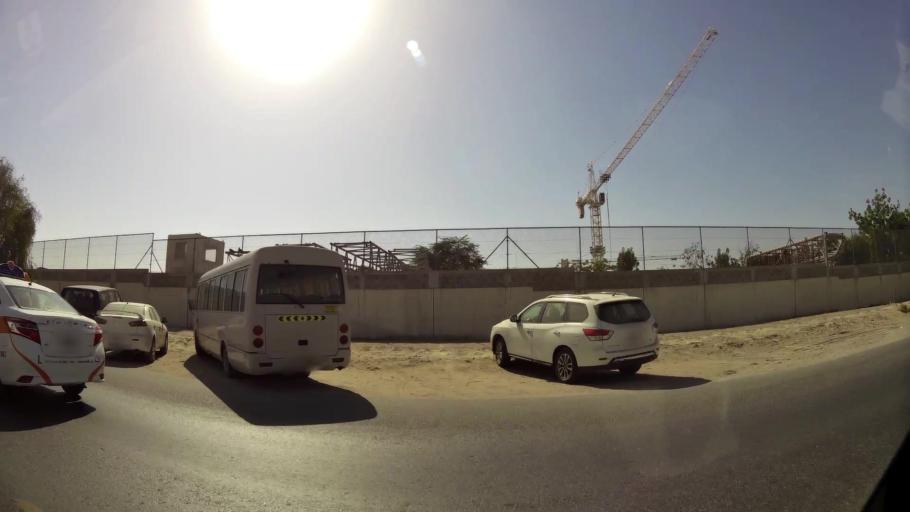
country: AE
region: Dubai
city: Dubai
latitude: 25.1257
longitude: 55.2232
